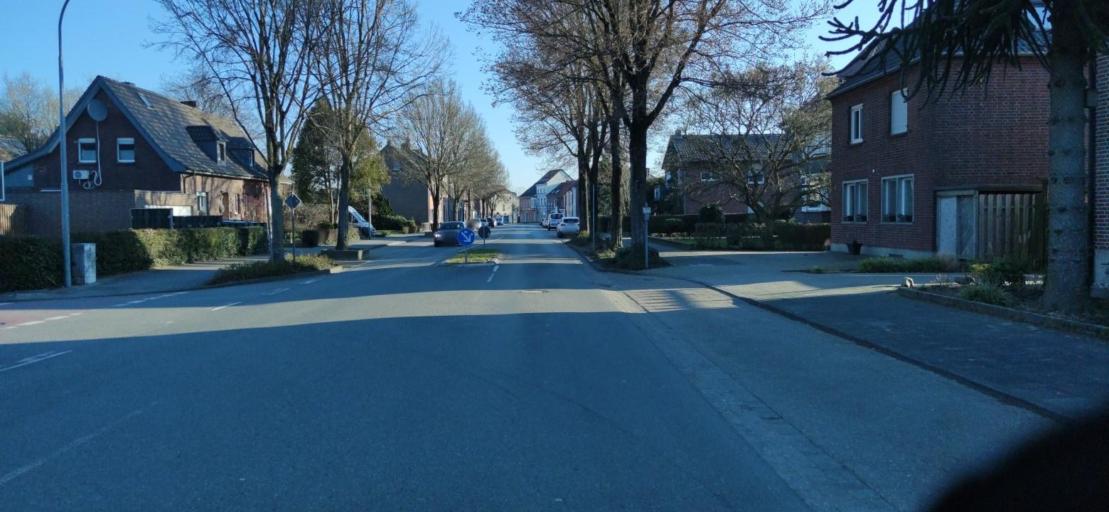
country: DE
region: North Rhine-Westphalia
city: Straelen
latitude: 51.4412
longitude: 6.2641
